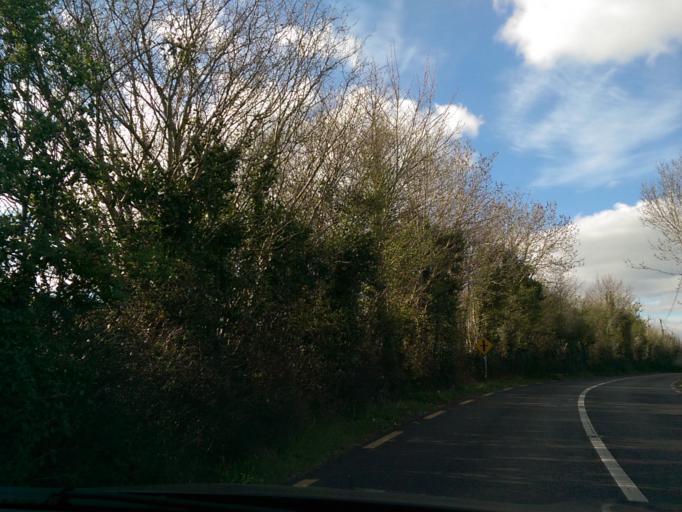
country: IE
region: Connaught
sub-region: County Galway
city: Portumna
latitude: 53.1230
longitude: -8.2433
